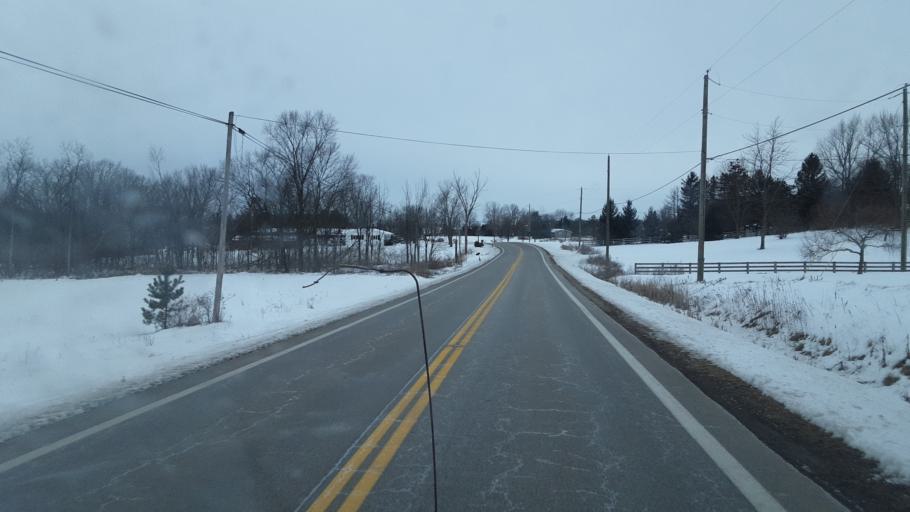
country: US
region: Ohio
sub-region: Union County
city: Marysville
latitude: 40.1752
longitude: -83.3280
